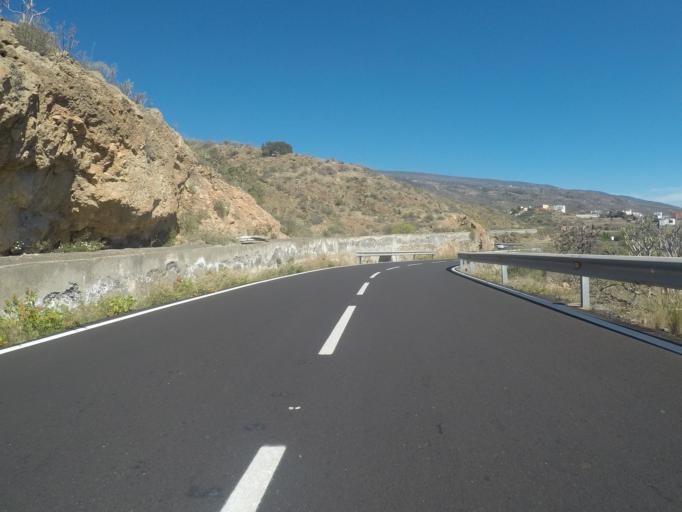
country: ES
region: Canary Islands
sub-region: Provincia de Santa Cruz de Tenerife
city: Lomo de Arico
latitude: 28.1780
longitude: -16.4870
